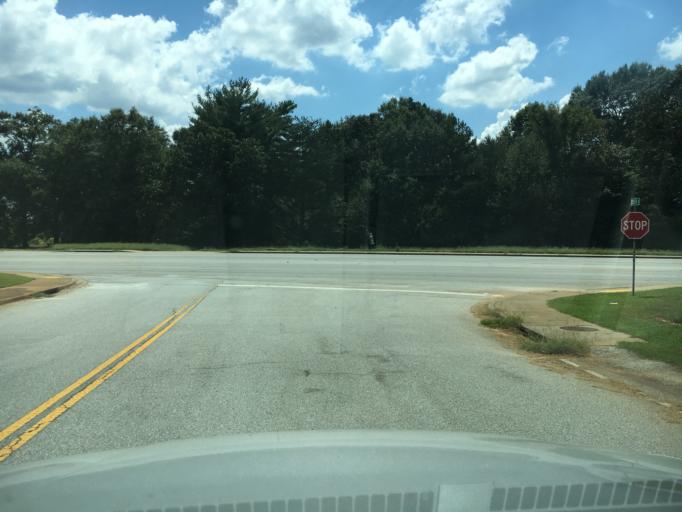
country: US
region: South Carolina
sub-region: Spartanburg County
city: Wellford
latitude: 34.8823
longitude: -82.0597
